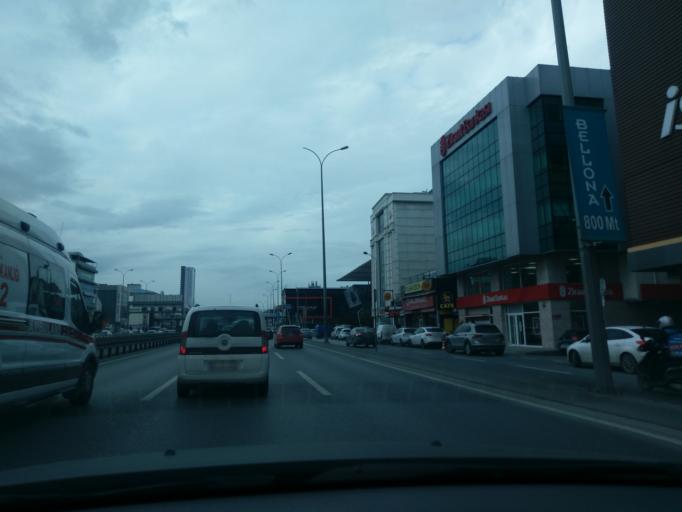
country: TR
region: Istanbul
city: Yakuplu
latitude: 40.9896
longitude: 28.7158
